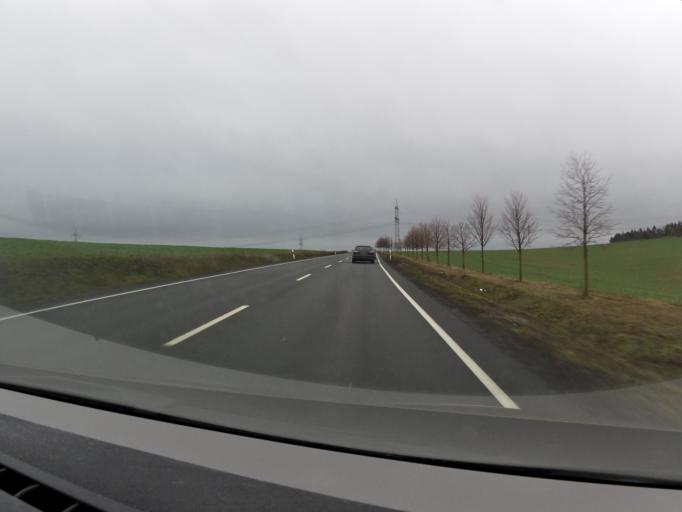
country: DE
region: Saxony-Anhalt
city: Grossorner
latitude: 51.6239
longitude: 11.4748
